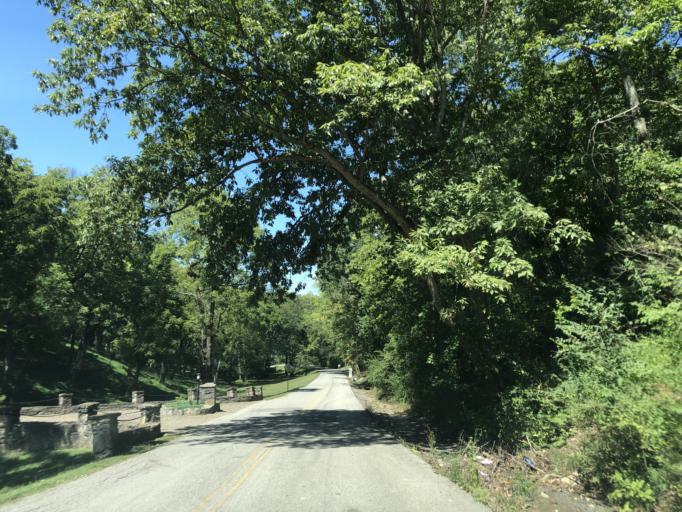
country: US
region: Tennessee
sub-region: Davidson County
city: Oak Hill
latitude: 36.0747
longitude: -86.7890
